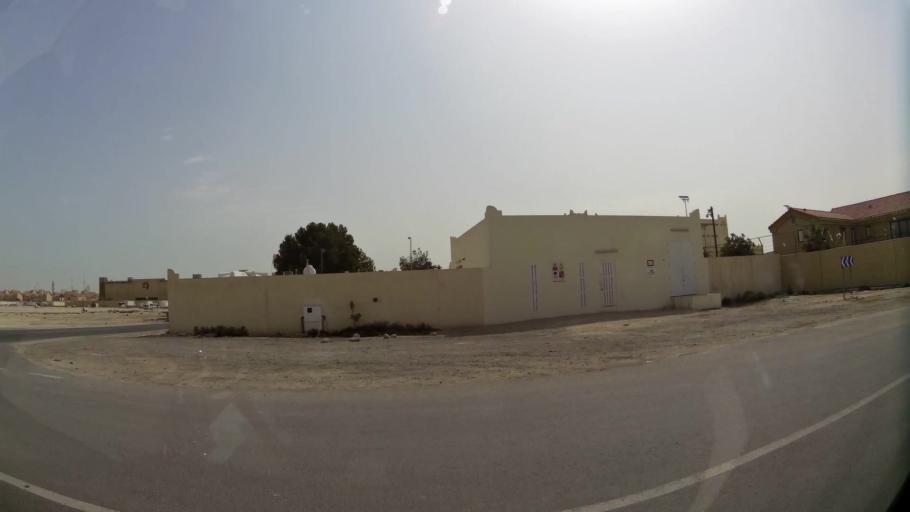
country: QA
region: Baladiyat ad Dawhah
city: Doha
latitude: 25.2997
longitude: 51.4850
